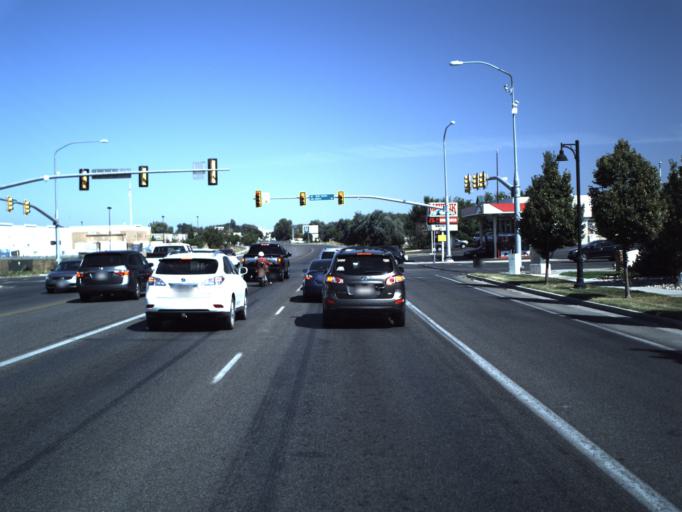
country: US
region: Utah
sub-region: Cache County
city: Providence
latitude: 41.7096
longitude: -111.8345
